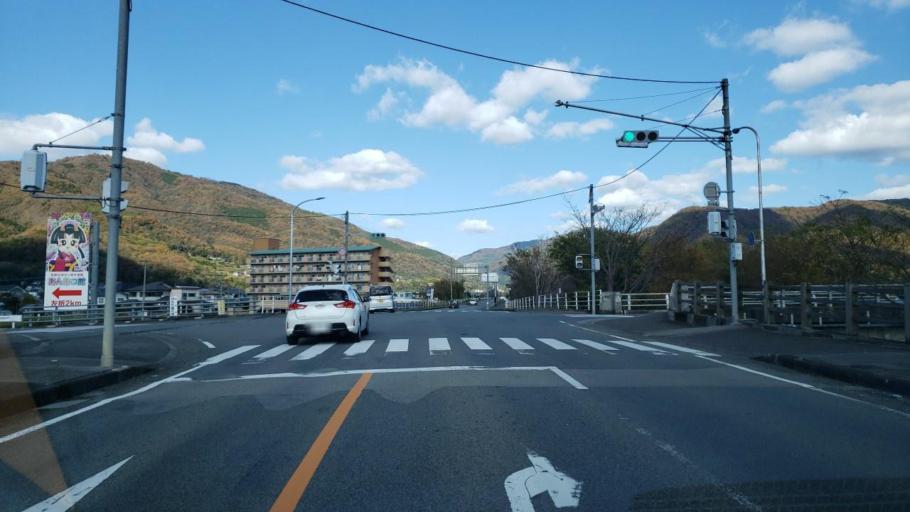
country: JP
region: Tokushima
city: Wakimachi
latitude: 34.0778
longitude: 134.1728
